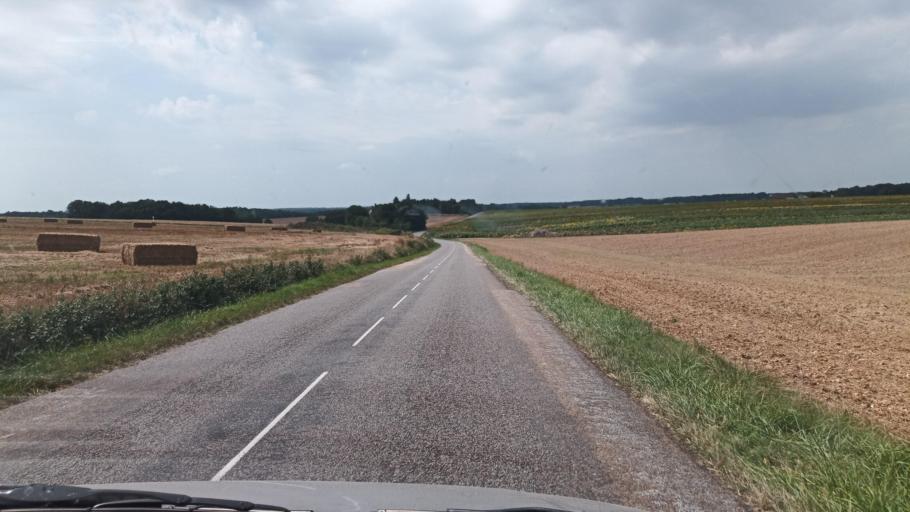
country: FR
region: Bourgogne
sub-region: Departement de l'Yonne
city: Egriselles-le-Bocage
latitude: 48.0366
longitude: 3.1956
